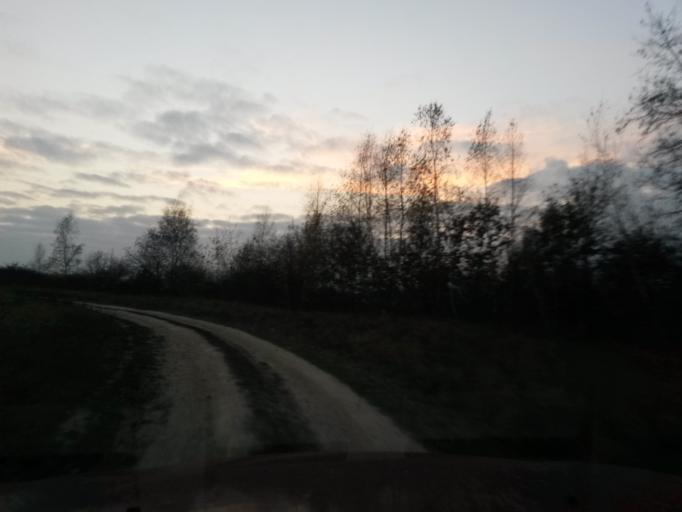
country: SK
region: Kosicky
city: Kosice
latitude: 48.7137
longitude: 21.2918
